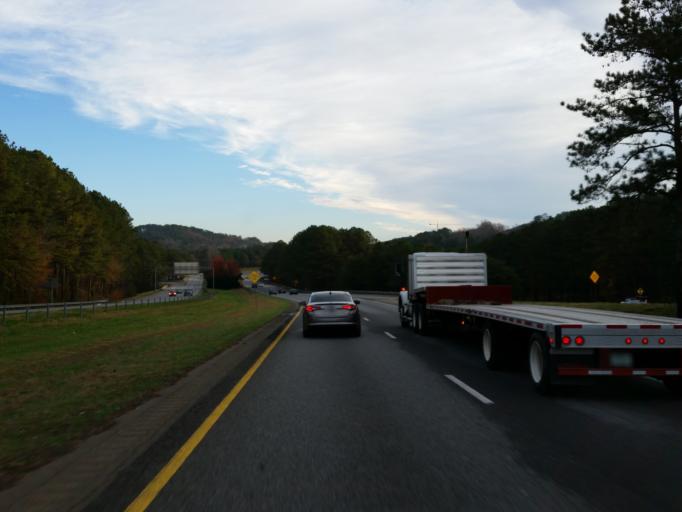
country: US
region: Georgia
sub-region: Cherokee County
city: Canton
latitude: 34.2217
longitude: -84.4869
